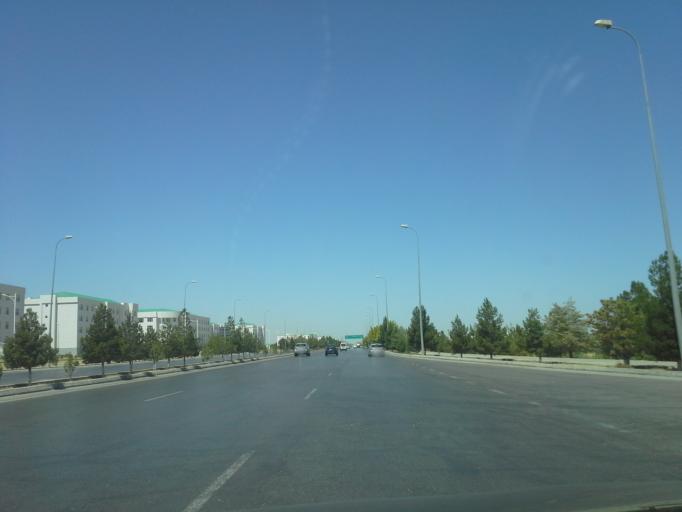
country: TM
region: Ahal
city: Ashgabat
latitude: 37.9819
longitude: 58.3353
